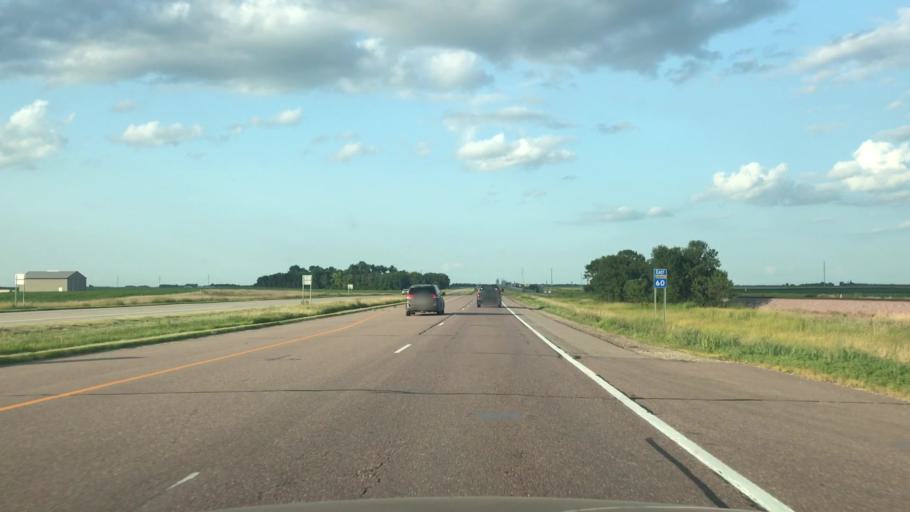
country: US
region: Minnesota
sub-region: Nobles County
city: Worthington
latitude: 43.6605
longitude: -95.5302
